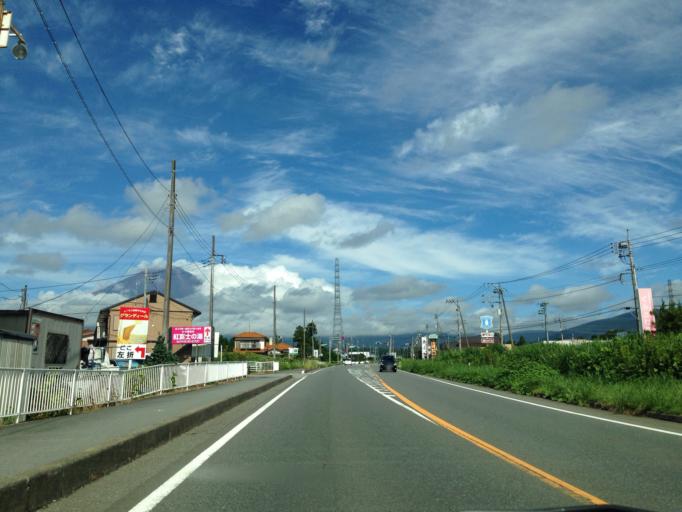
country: JP
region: Shizuoka
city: Gotemba
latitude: 35.3141
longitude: 138.9240
